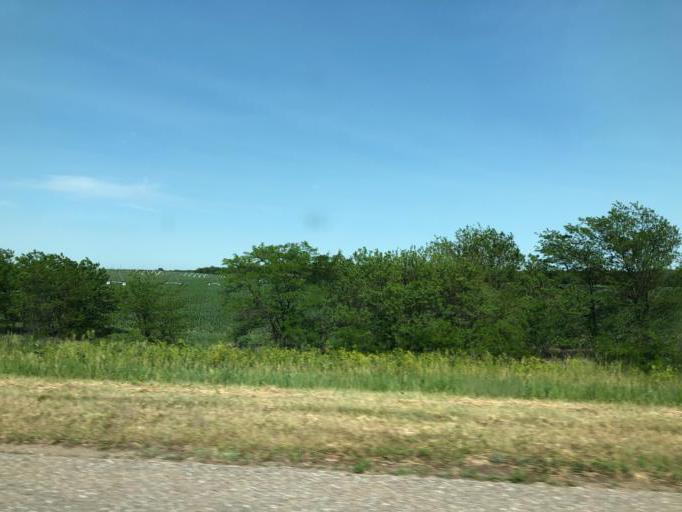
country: US
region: Nebraska
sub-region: Fillmore County
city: Geneva
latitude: 40.5478
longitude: -97.5877
